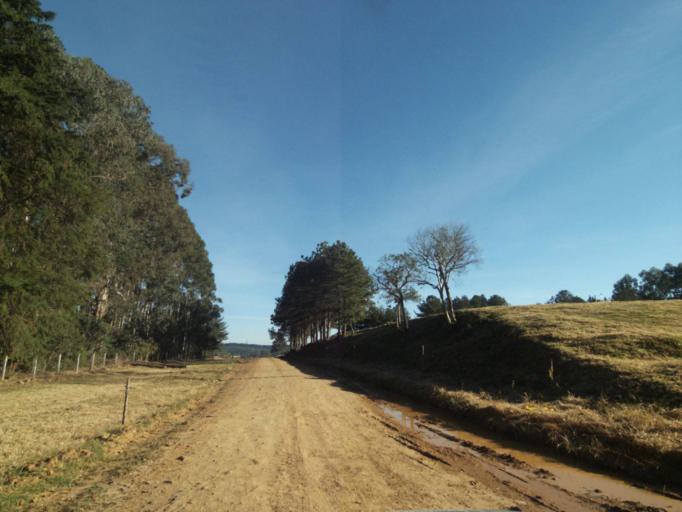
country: BR
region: Parana
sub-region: Telemaco Borba
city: Telemaco Borba
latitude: -24.5135
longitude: -50.6612
